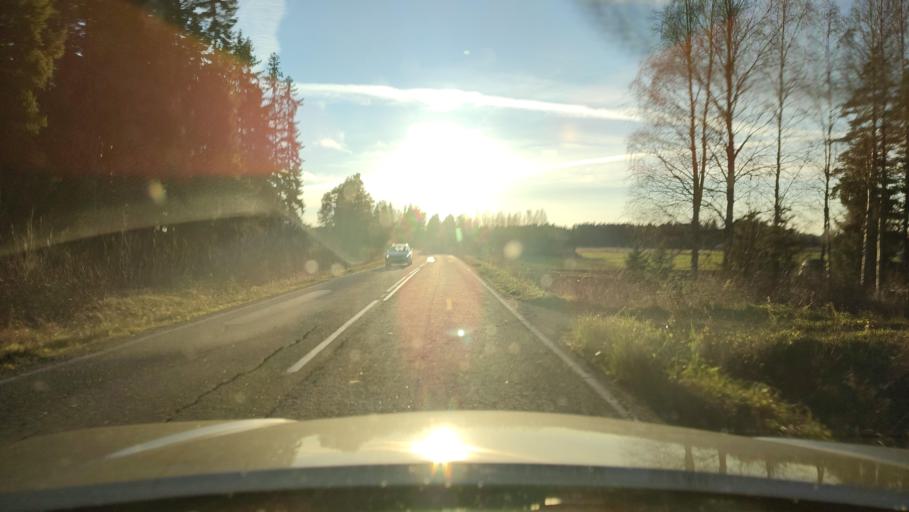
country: FI
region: Ostrobothnia
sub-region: Vaasa
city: Malax
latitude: 62.6917
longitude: 21.5569
